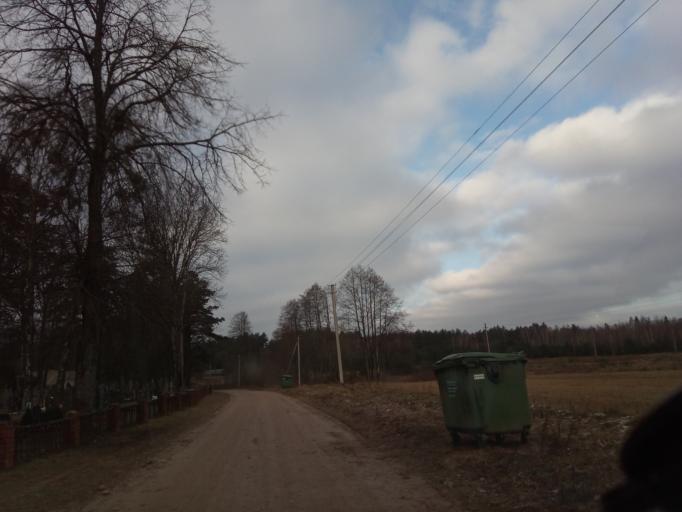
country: LT
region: Alytaus apskritis
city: Druskininkai
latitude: 53.9554
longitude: 24.2921
